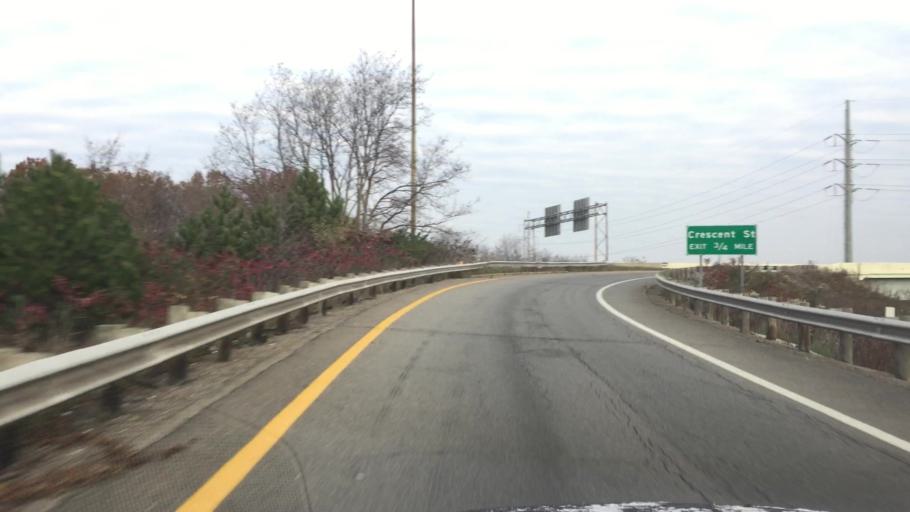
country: US
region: Ohio
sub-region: Mahoning County
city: Youngstown
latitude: 41.1045
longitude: -80.6766
